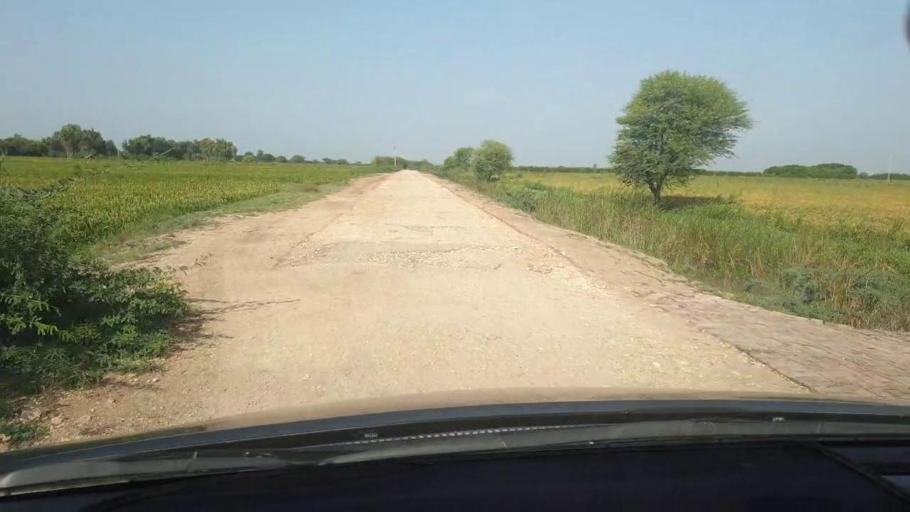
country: PK
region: Sindh
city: Tando Bago
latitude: 24.6741
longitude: 69.1797
